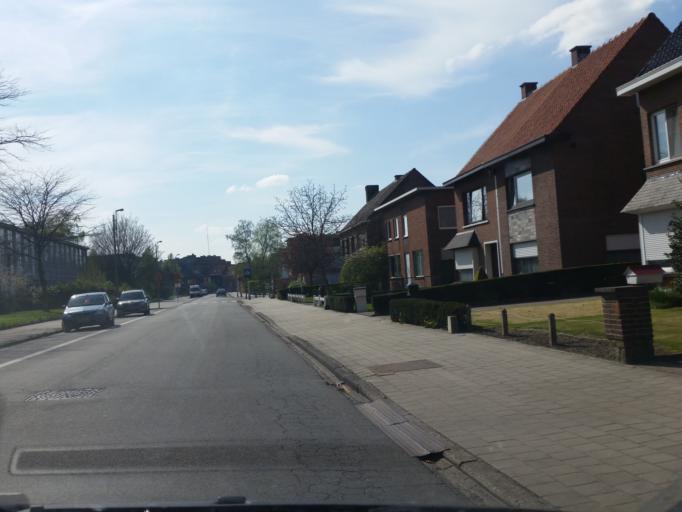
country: BE
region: Flanders
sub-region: Provincie Oost-Vlaanderen
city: Sint-Niklaas
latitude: 51.1740
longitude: 4.1450
